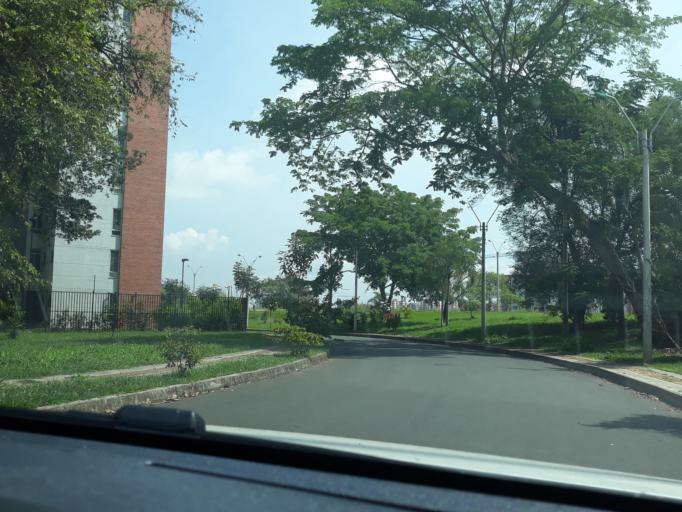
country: CO
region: Valle del Cauca
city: Cali
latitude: 3.3649
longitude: -76.5115
